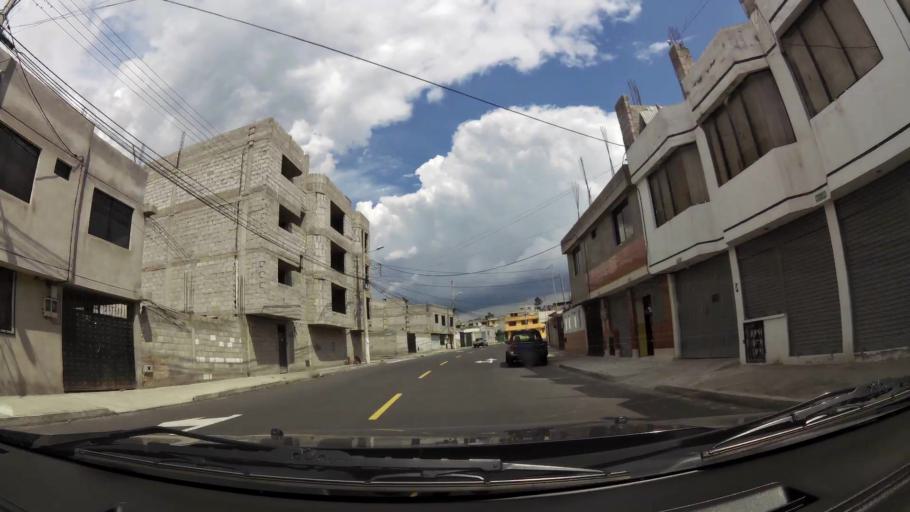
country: EC
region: Pichincha
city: Quito
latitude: -0.0981
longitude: -78.4547
